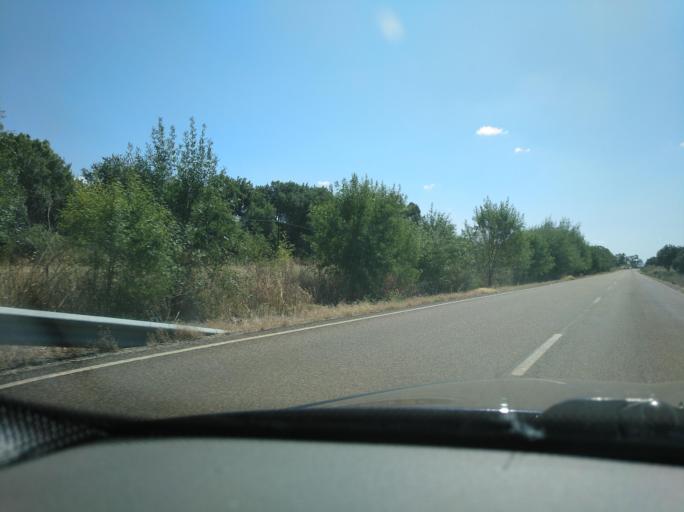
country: ES
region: Extremadura
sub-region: Provincia de Badajoz
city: Olivenza
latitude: 38.7171
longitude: -7.1986
